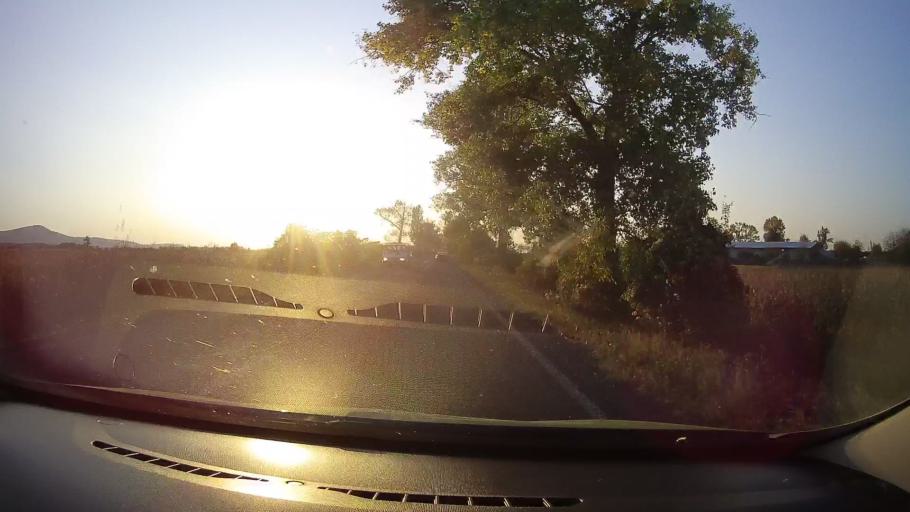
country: RO
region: Arad
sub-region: Comuna Ineu
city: Ineu
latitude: 46.4290
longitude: 21.8925
